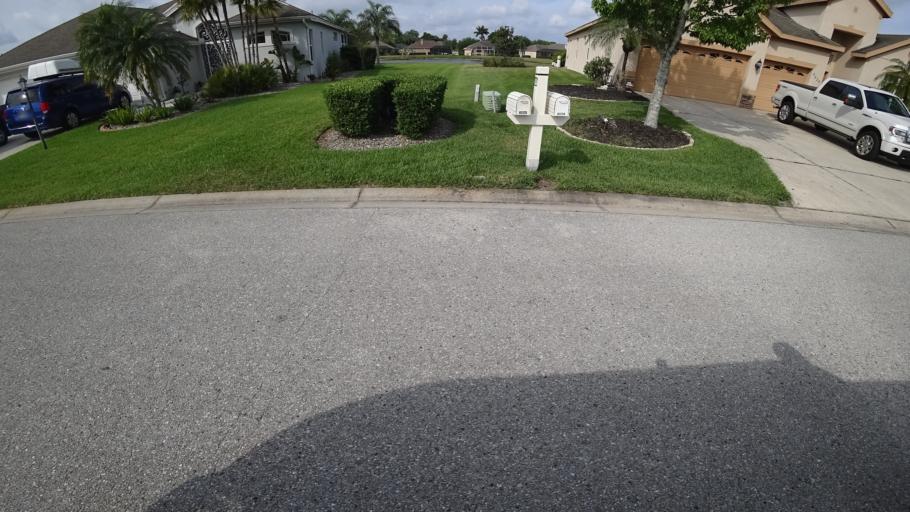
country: US
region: Florida
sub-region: Manatee County
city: Ellenton
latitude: 27.5689
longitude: -82.4722
